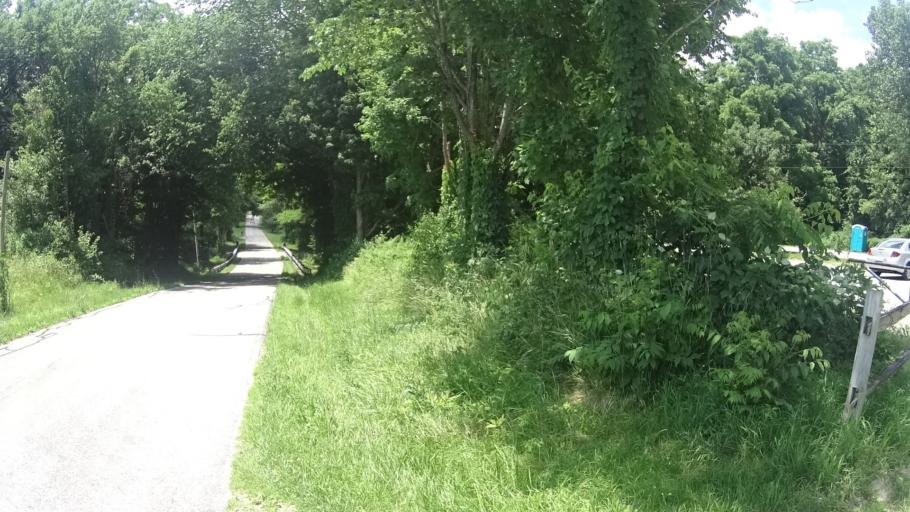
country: US
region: Ohio
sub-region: Erie County
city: Huron
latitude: 41.3191
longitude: -82.5264
